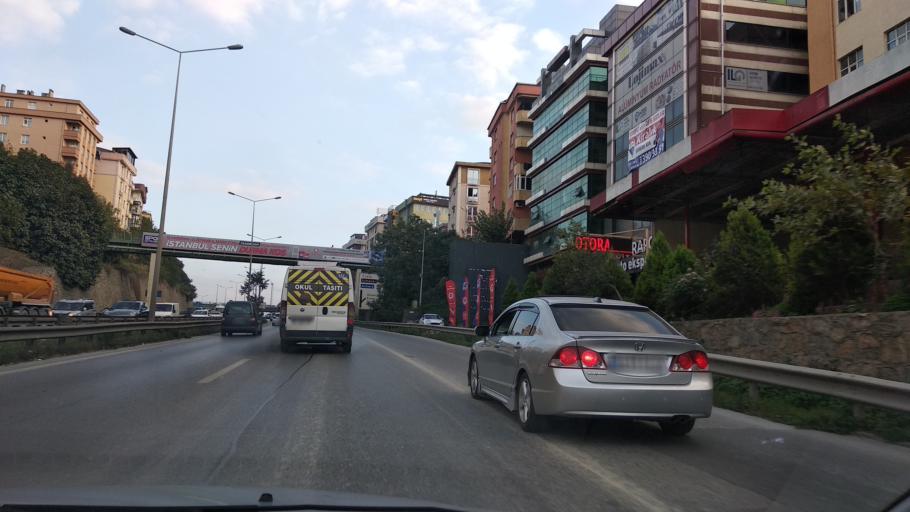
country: TR
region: Istanbul
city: Pendik
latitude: 40.8619
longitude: 29.2778
